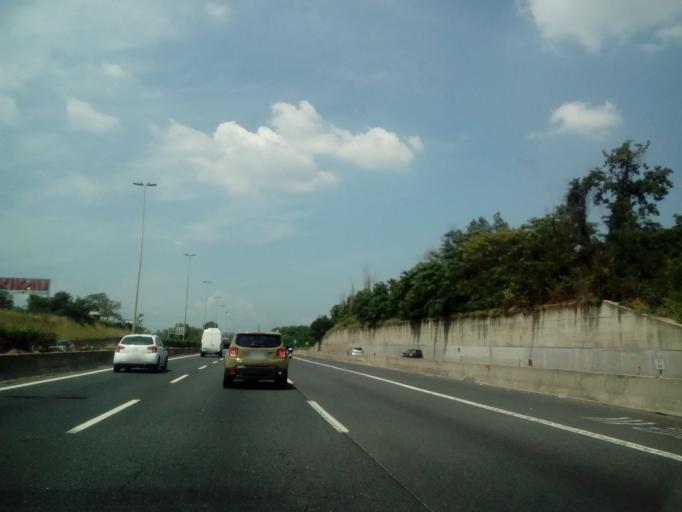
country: IT
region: Latium
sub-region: Citta metropolitana di Roma Capitale
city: Setteville
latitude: 41.8944
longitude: 12.6153
